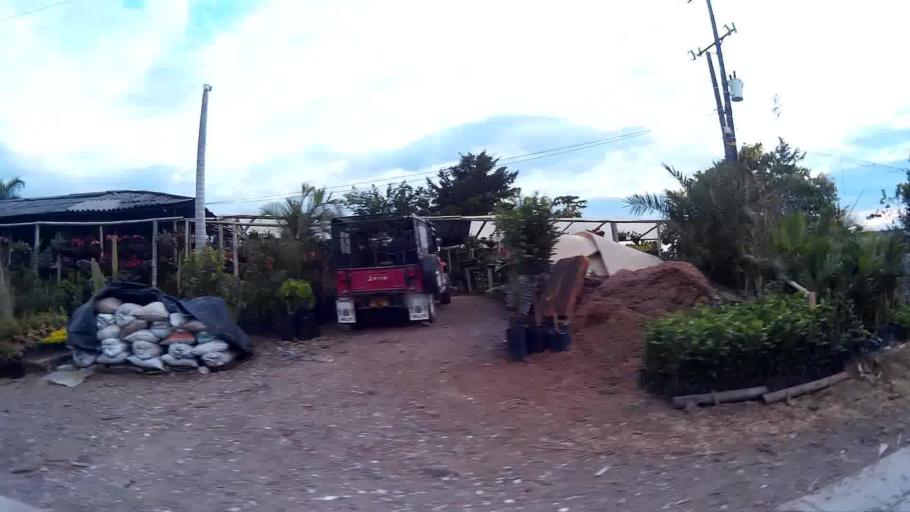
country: CO
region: Risaralda
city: Pereira
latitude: 4.7610
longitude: -75.6839
